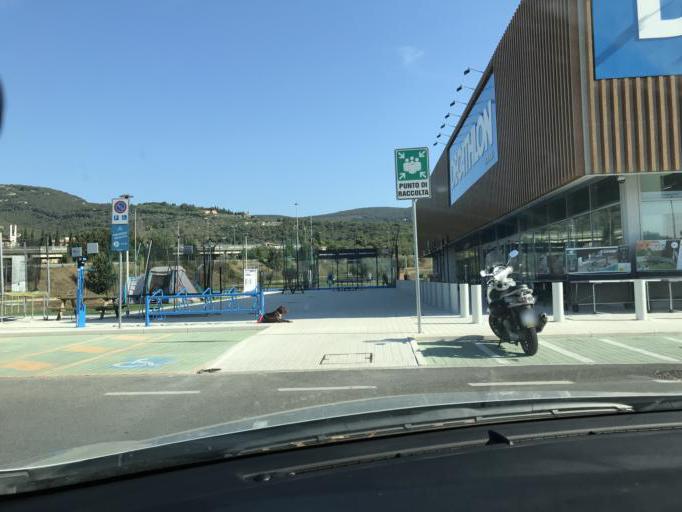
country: IT
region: Umbria
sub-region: Provincia di Perugia
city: Lacugnano
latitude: 43.1019
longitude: 12.3230
